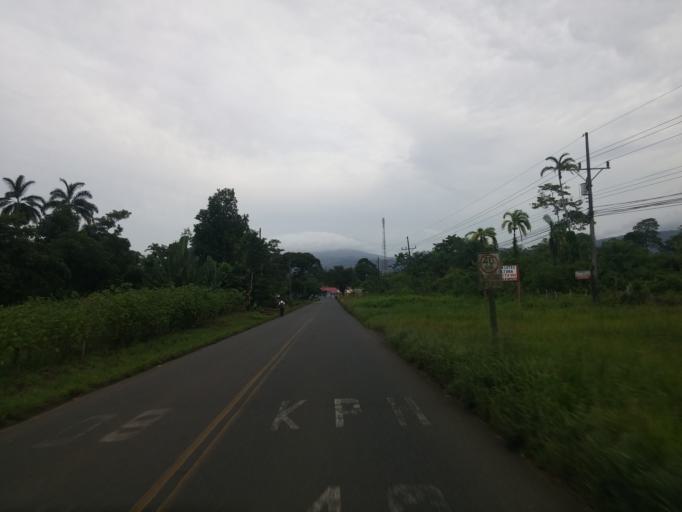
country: CR
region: Alajuela
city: Upala
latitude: 10.8435
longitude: -85.0417
